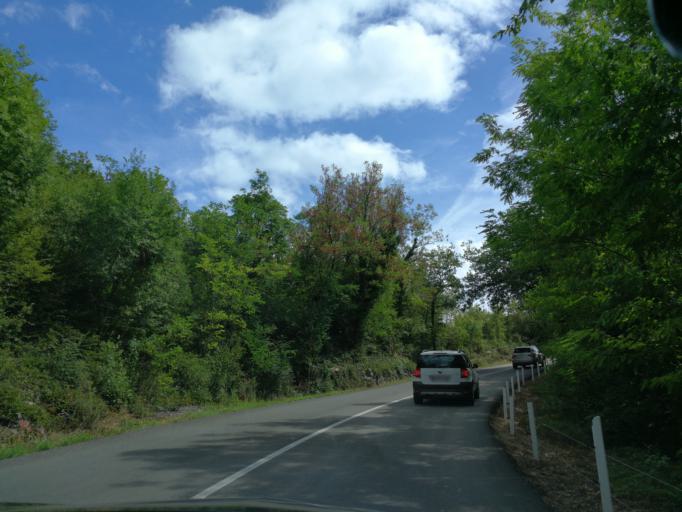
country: HR
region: Primorsko-Goranska
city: Punat
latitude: 45.0806
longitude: 14.6531
